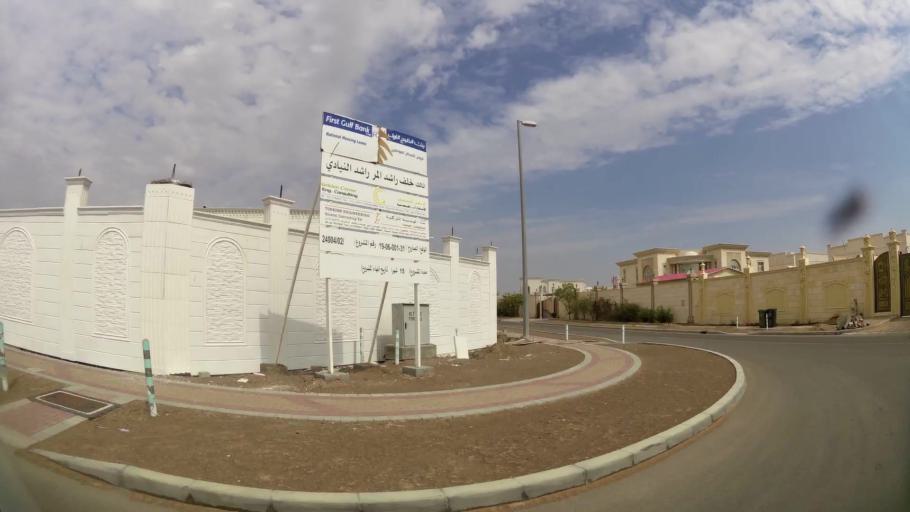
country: AE
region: Abu Dhabi
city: Al Ain
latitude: 24.1900
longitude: 55.8071
